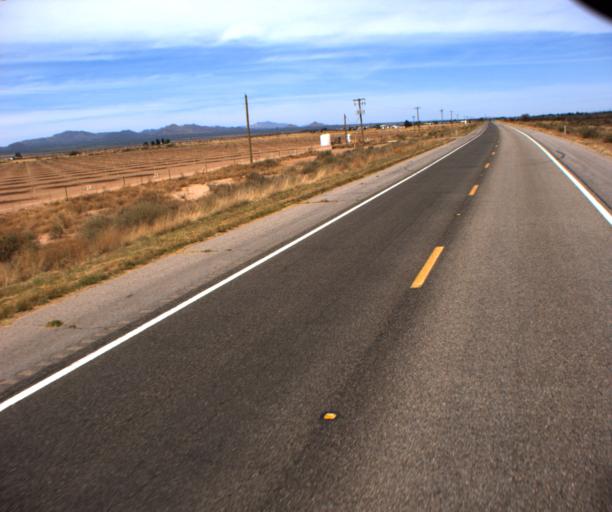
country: US
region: Arizona
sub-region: Cochise County
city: Pirtleville
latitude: 31.6533
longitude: -109.6746
